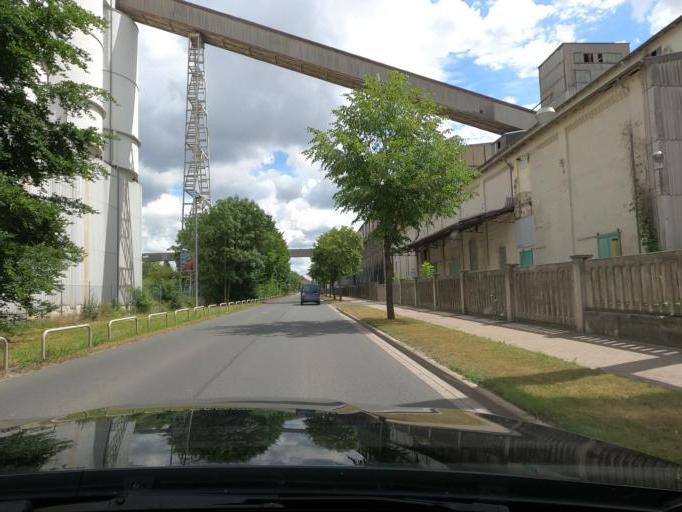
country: DE
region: Lower Saxony
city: Sehnde
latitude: 52.3517
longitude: 9.8859
